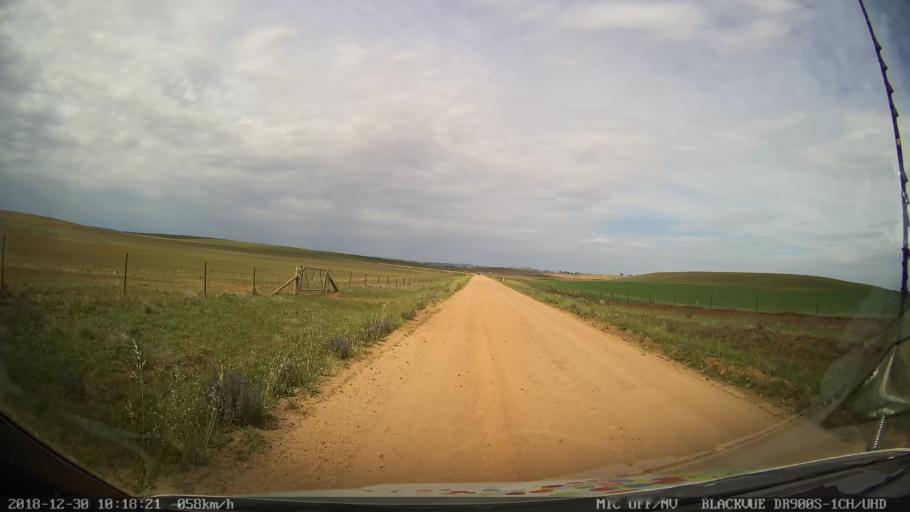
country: AU
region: New South Wales
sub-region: Snowy River
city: Berridale
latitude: -36.5515
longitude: 149.0100
